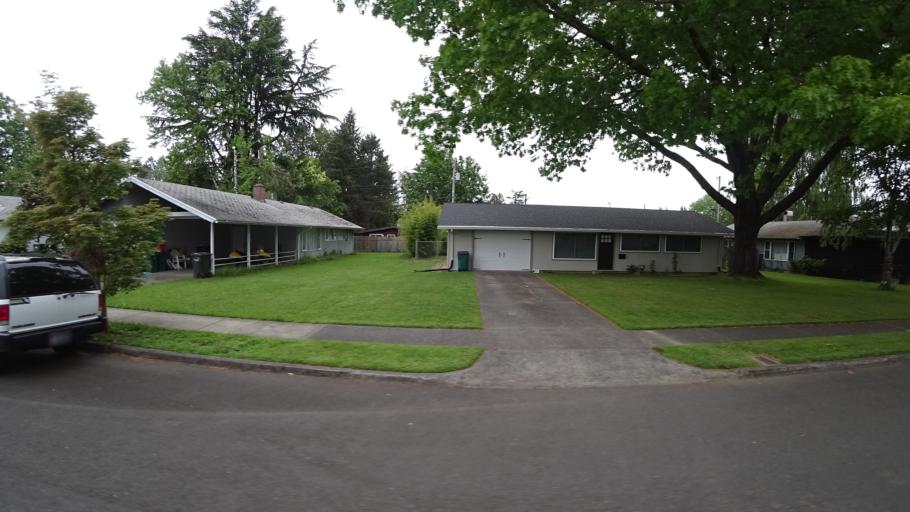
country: US
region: Oregon
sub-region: Washington County
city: Beaverton
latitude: 45.4781
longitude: -122.8026
